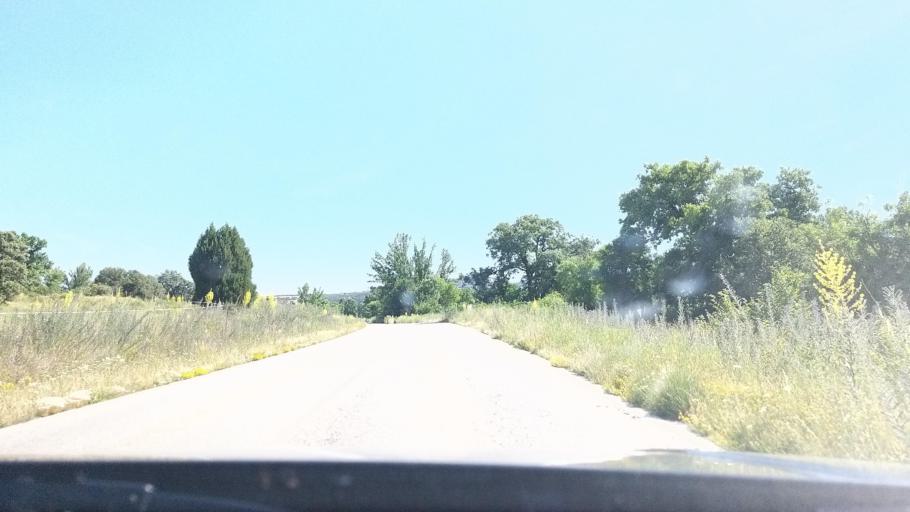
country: ES
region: Castille and Leon
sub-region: Provincia de Segovia
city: Pedraza
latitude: 41.1373
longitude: -3.8331
